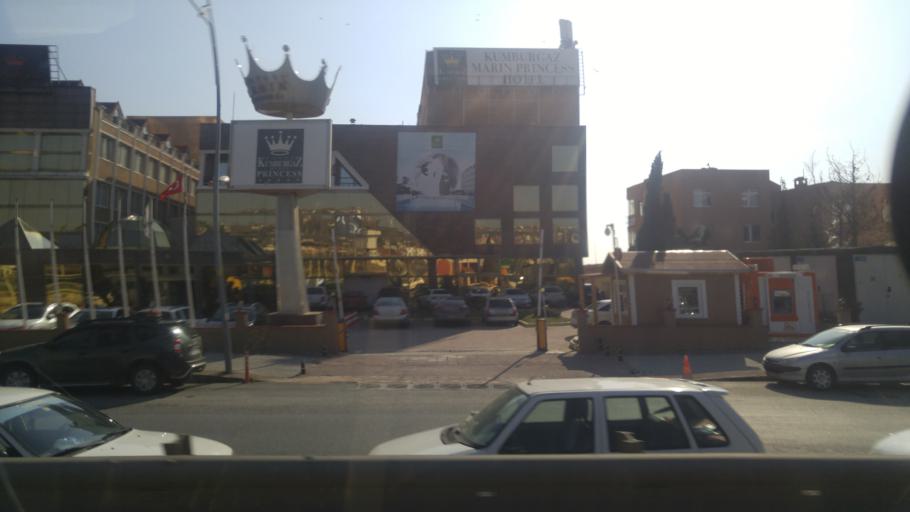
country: TR
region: Istanbul
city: Celaliye
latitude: 41.0373
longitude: 28.4375
